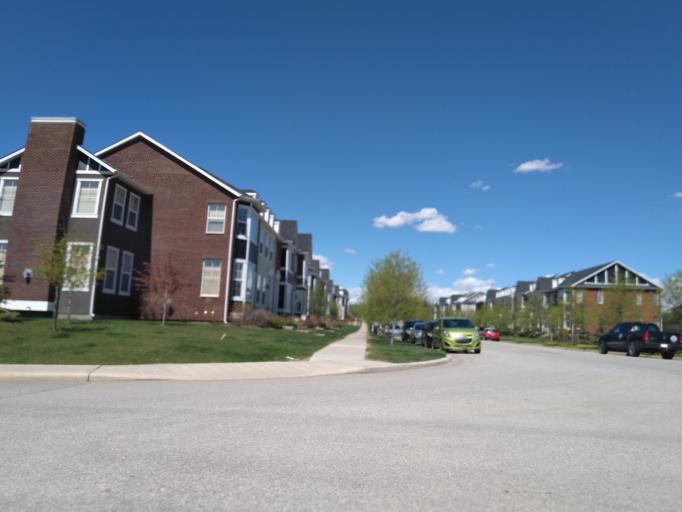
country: CA
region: Alberta
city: Chestermere
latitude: 51.0235
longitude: -113.8345
